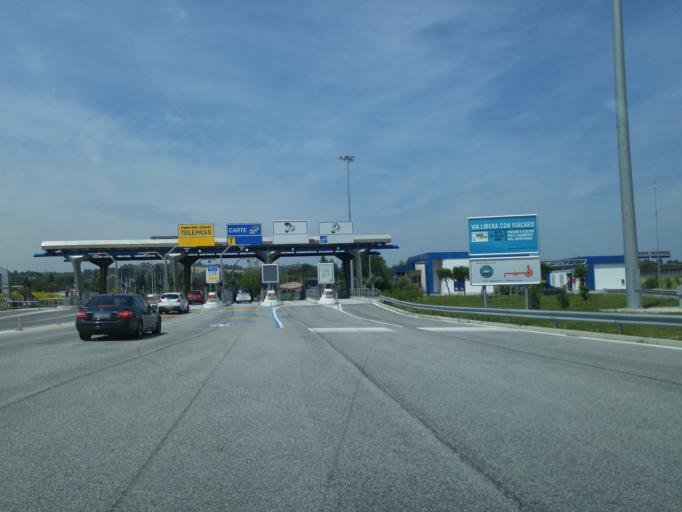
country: IT
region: The Marches
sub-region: Provincia di Ancona
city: Senigallia
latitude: 43.7022
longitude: 13.2103
